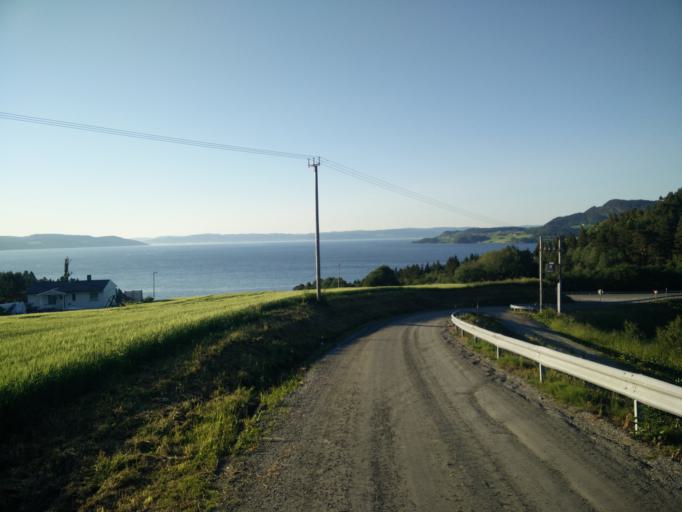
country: NO
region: Sor-Trondelag
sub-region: Skaun
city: Borsa
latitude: 63.3449
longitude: 10.0404
